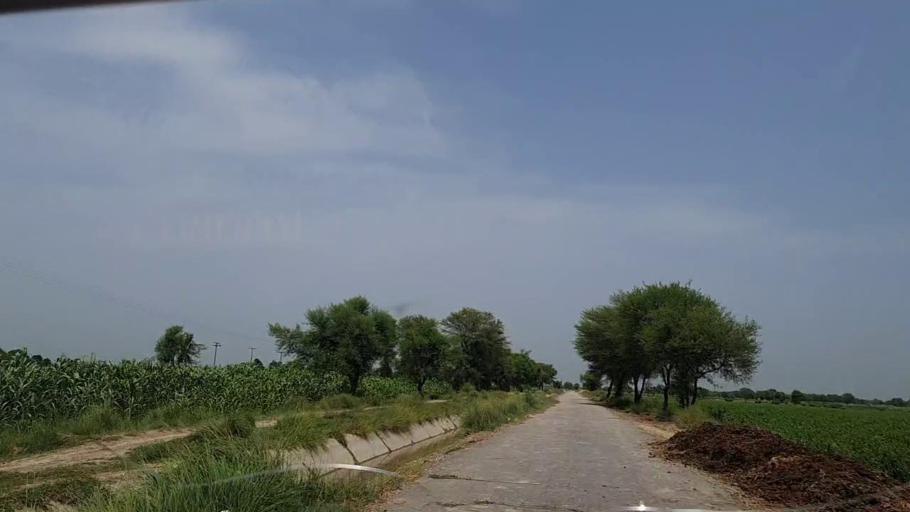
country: PK
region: Sindh
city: Tharu Shah
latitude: 26.9350
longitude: 68.0683
